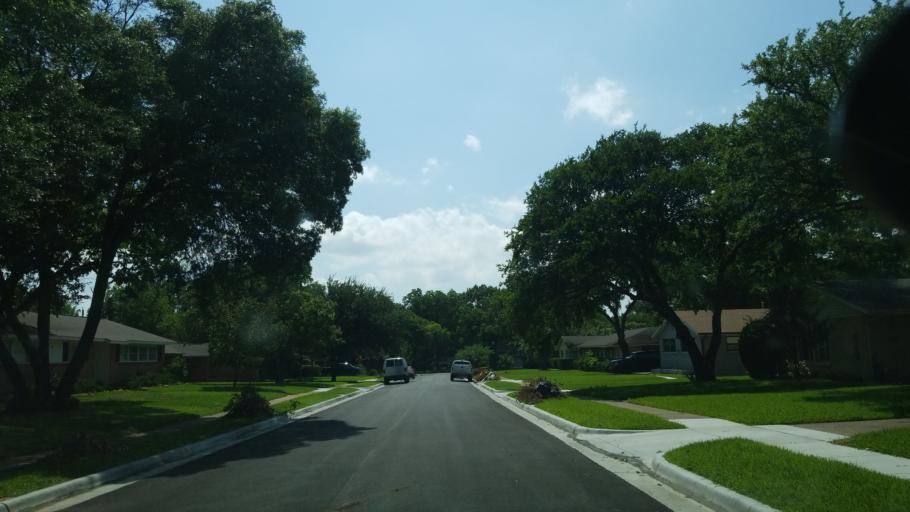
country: US
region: Texas
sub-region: Dallas County
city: Farmers Branch
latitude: 32.8837
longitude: -96.8592
